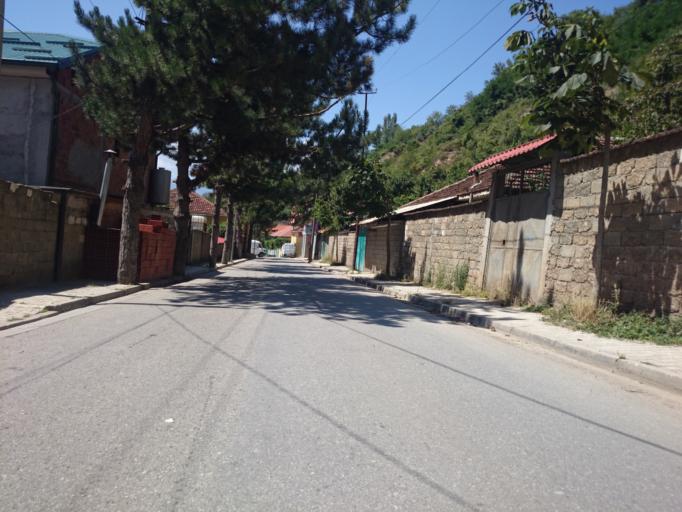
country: AL
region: Diber
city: Peshkopi
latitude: 41.6864
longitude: 20.4405
